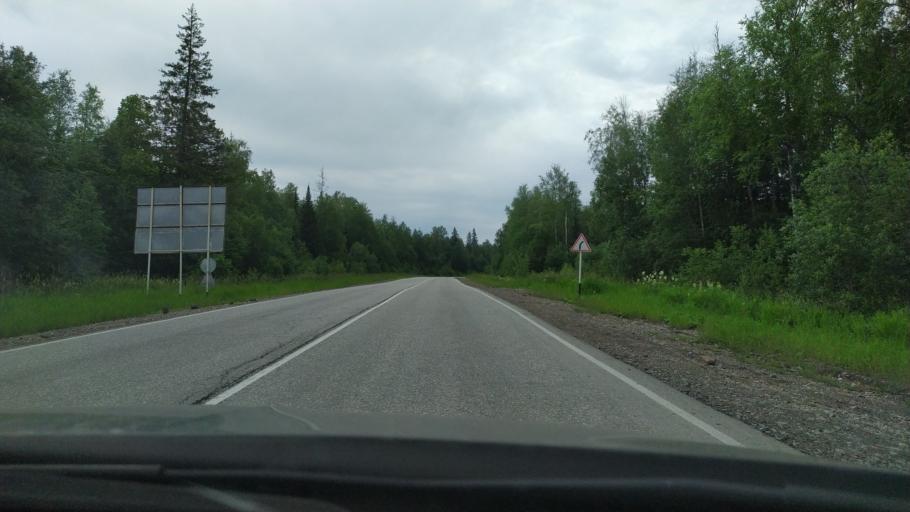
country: RU
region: Perm
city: Gremyachinsk
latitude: 58.4340
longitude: 57.8845
